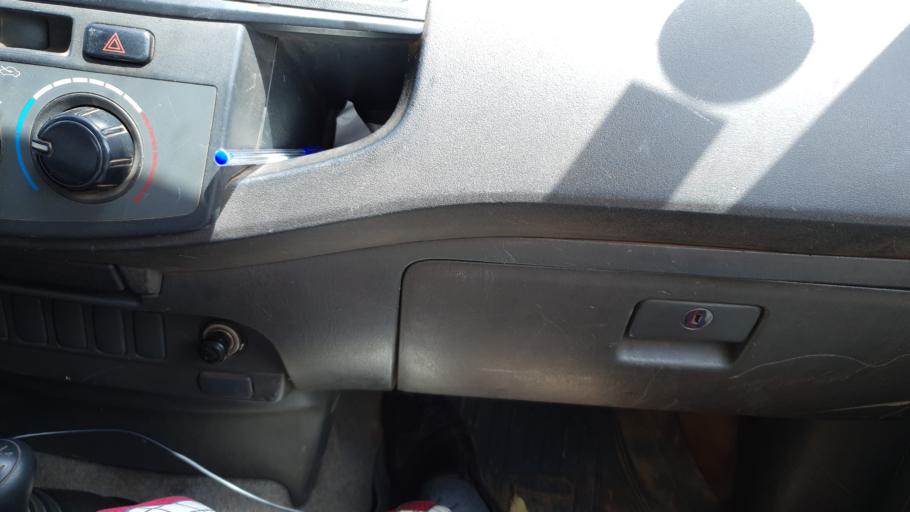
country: ML
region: Segou
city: Baroueli
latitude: 13.3367
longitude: -7.0861
